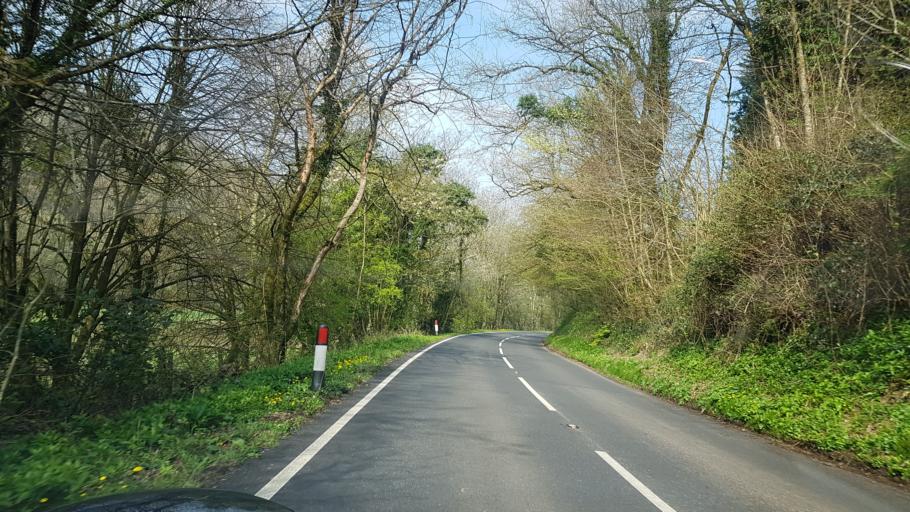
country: GB
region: Wales
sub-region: Monmouthshire
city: Monmouth
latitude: 51.7706
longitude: -2.6798
